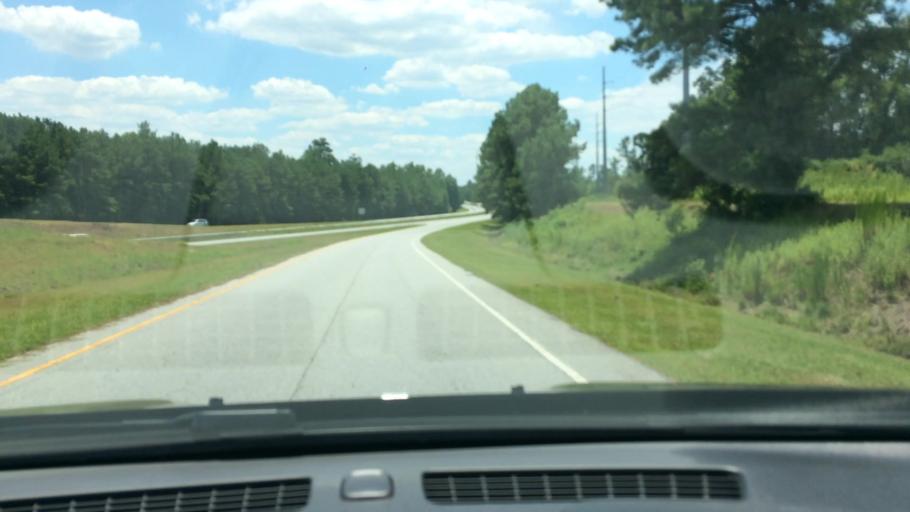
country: US
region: North Carolina
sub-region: Pitt County
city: Summerfield
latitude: 35.6280
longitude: -77.4349
